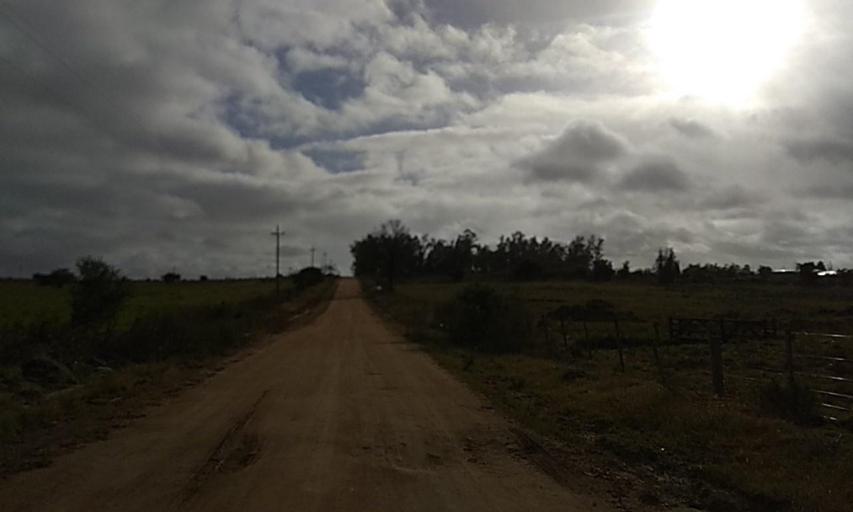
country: UY
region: Florida
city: Florida
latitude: -34.0599
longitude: -56.2289
